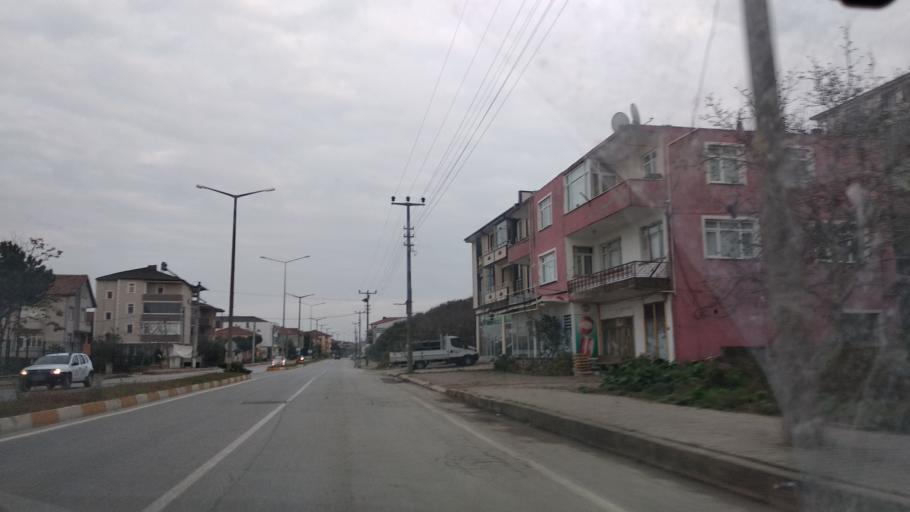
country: TR
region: Sakarya
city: Karasu
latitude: 41.0976
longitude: 30.6759
